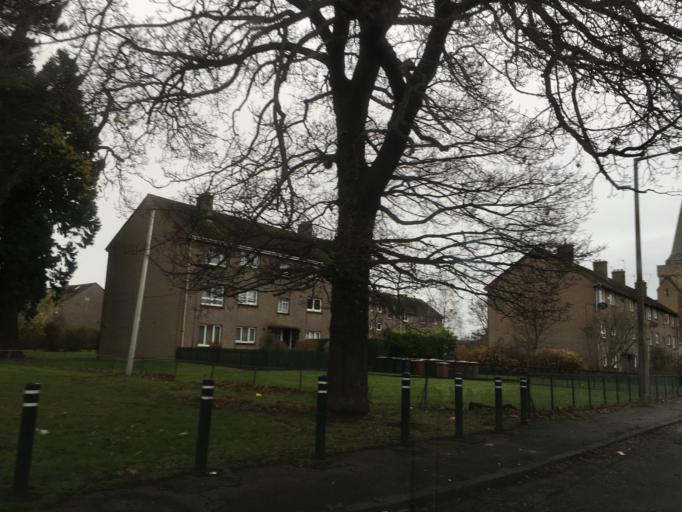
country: GB
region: Scotland
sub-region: Edinburgh
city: Colinton
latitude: 55.9305
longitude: -3.2638
